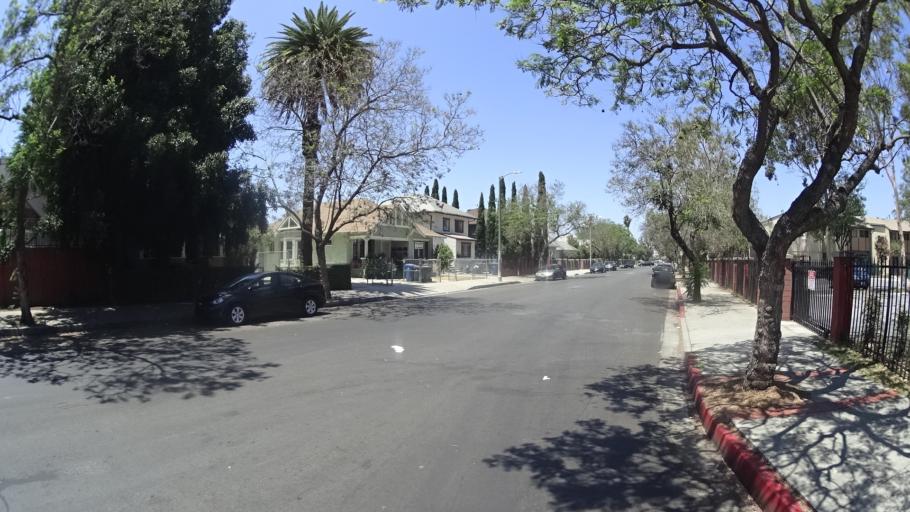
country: US
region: California
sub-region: Los Angeles County
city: Los Angeles
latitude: 34.0242
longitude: -118.2925
